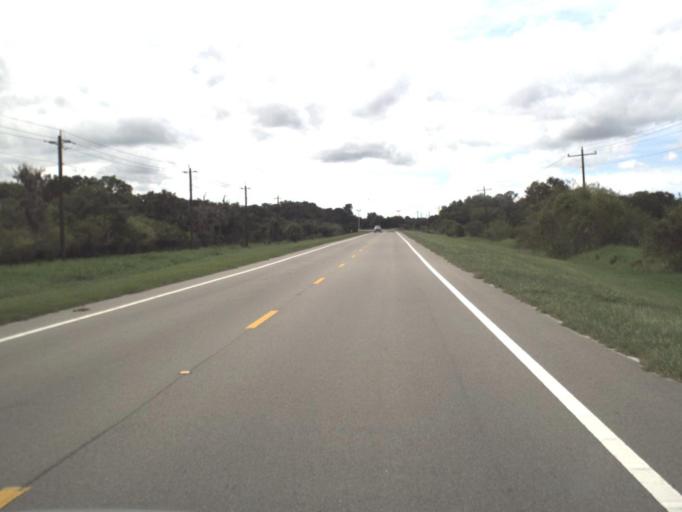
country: US
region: Florida
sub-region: Hillsborough County
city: Sun City Center
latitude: 27.5936
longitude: -82.3771
